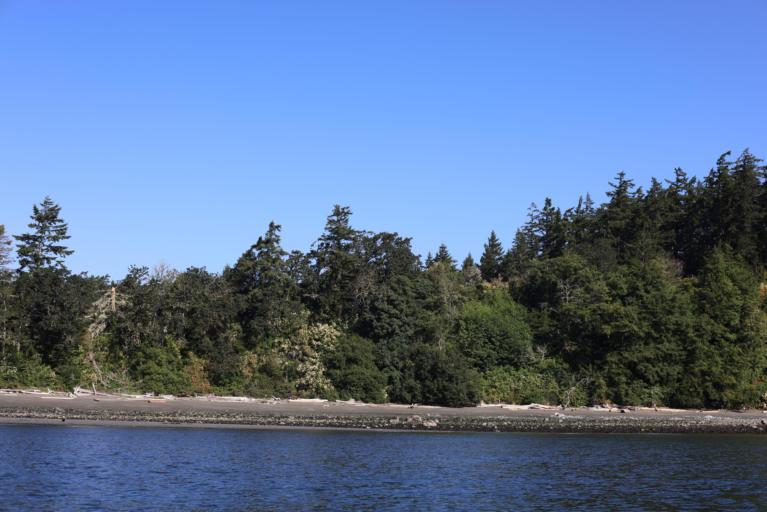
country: CA
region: British Columbia
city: Metchosin
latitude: 48.3693
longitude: -123.5278
